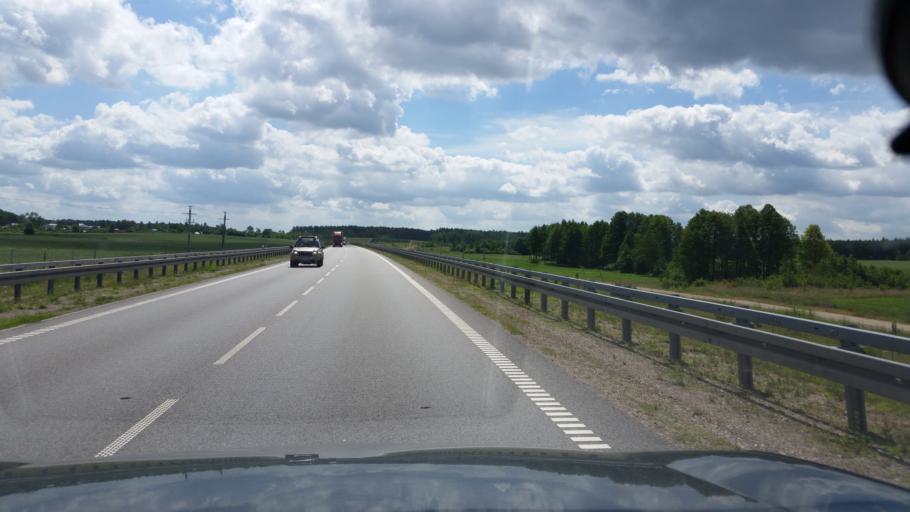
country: PL
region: Podlasie
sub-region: Powiat kolnenski
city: Stawiski
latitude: 53.3708
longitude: 22.1488
